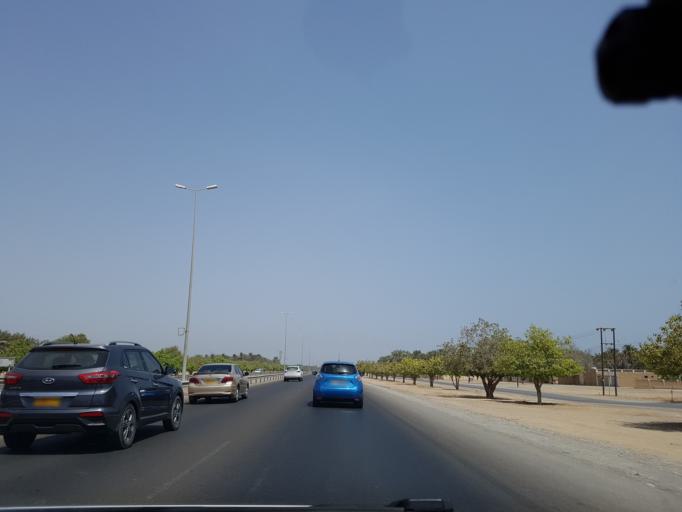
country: OM
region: Al Batinah
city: Saham
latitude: 24.1673
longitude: 56.8616
